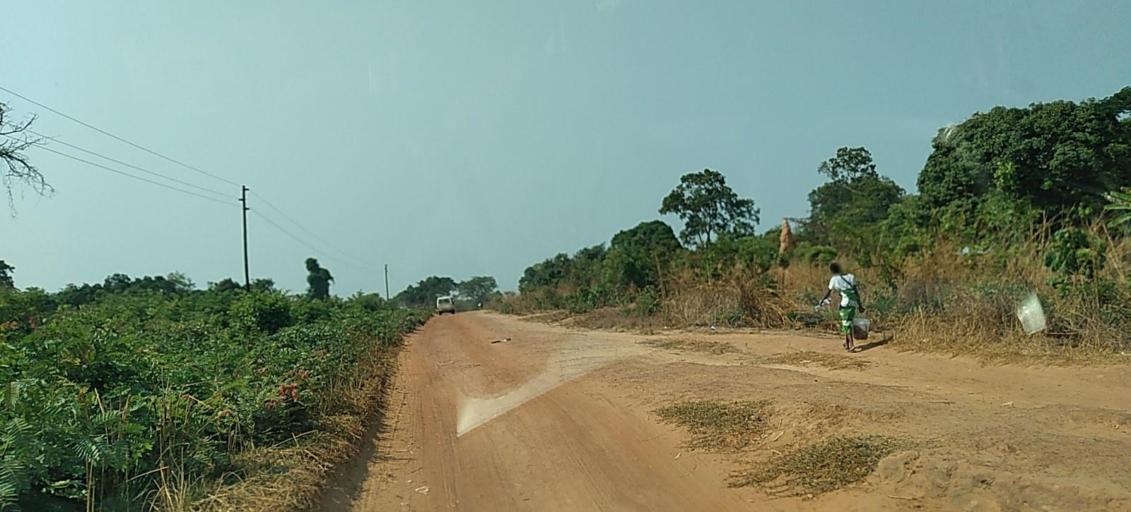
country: ZM
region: Copperbelt
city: Chingola
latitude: -12.9191
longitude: 27.3732
